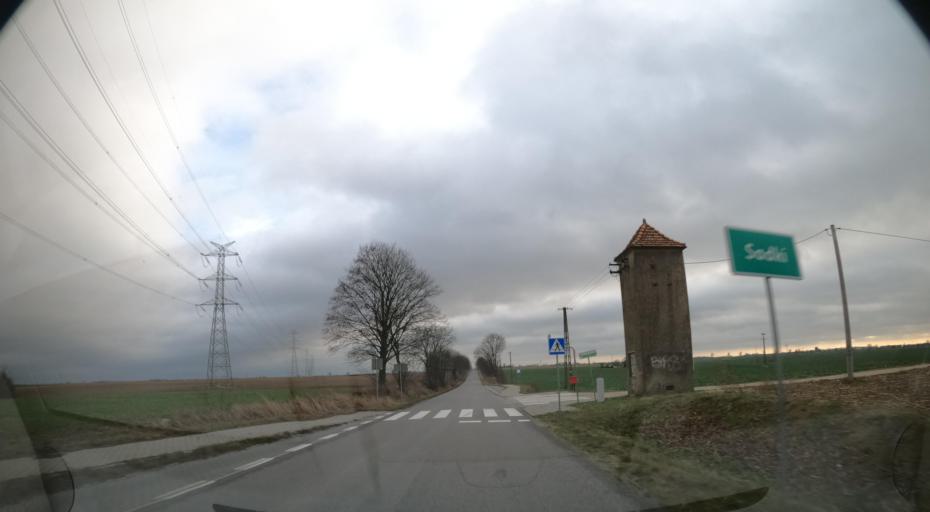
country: PL
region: Kujawsko-Pomorskie
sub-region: Powiat nakielski
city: Sadki
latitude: 53.1776
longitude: 17.4154
